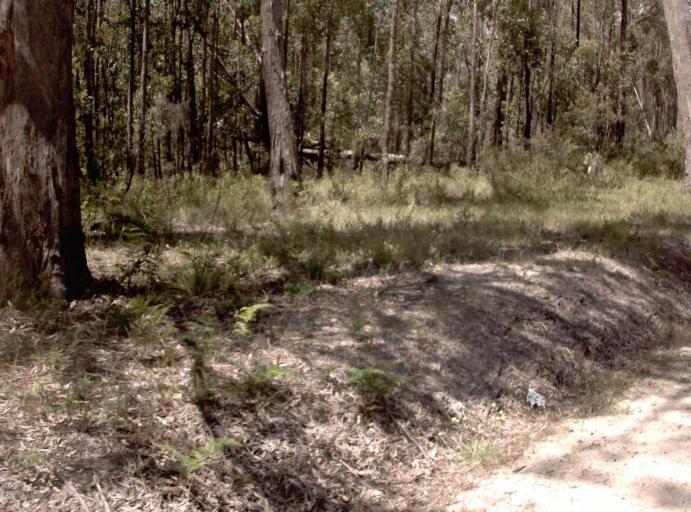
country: AU
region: New South Wales
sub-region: Bombala
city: Bombala
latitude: -37.5644
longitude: 149.1731
